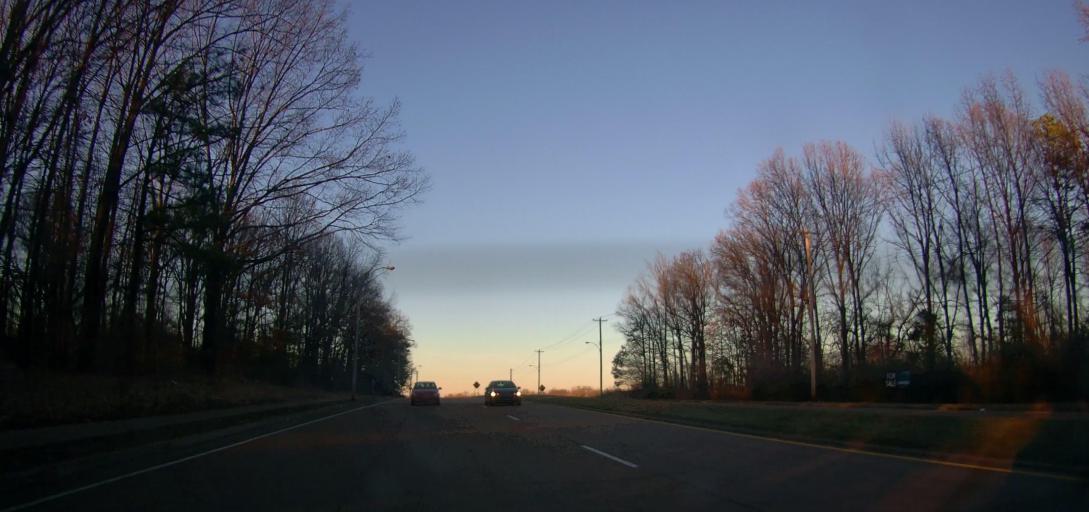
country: US
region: Tennessee
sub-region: Shelby County
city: Bartlett
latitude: 35.2391
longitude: -89.8975
